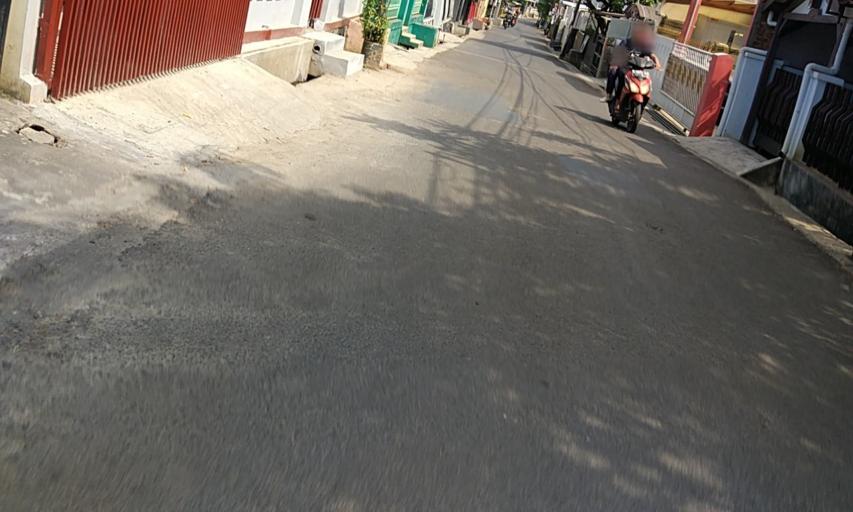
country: ID
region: West Java
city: Bandung
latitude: -6.9045
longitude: 107.6870
